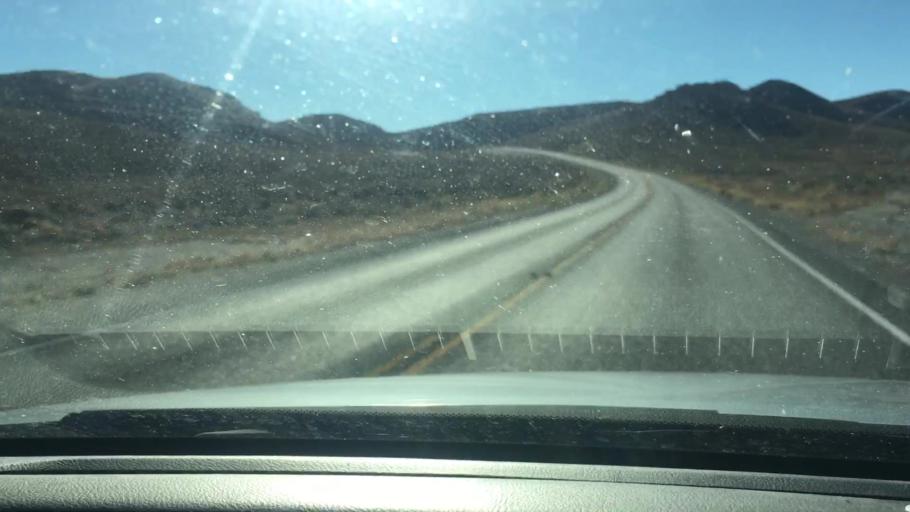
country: US
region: Nevada
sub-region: Nye County
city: Tonopah
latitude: 38.1195
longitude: -116.8946
